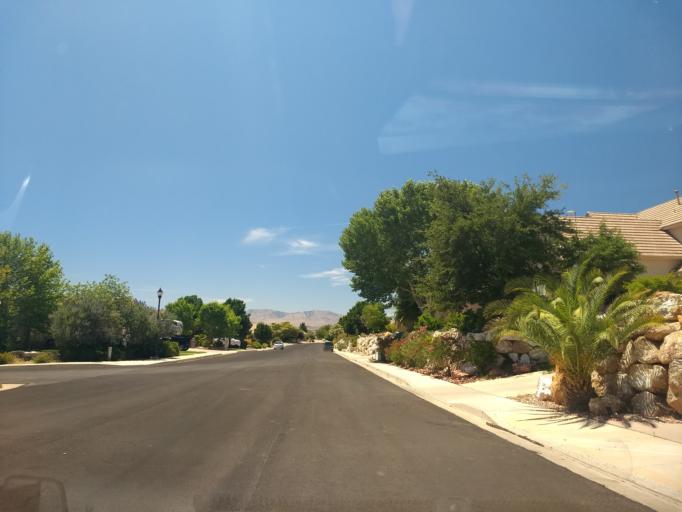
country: US
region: Utah
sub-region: Washington County
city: Washington
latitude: 37.0878
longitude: -113.4843
